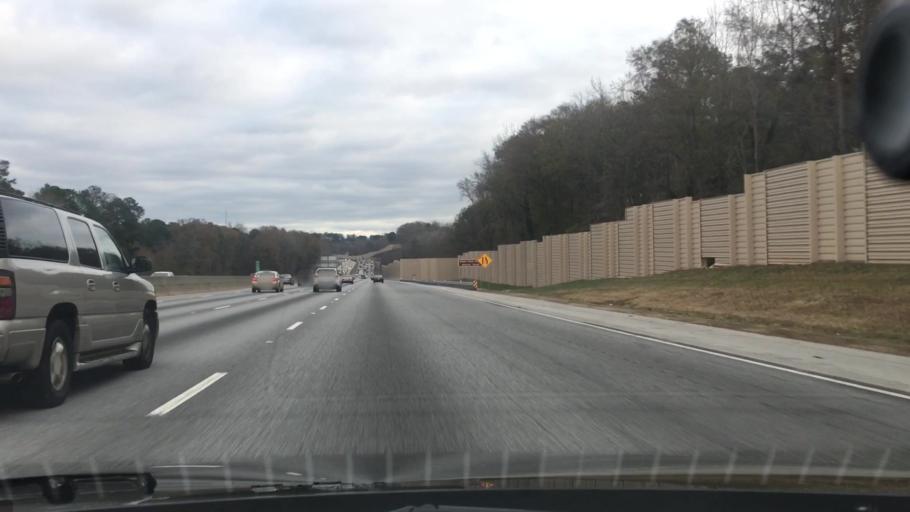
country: US
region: Georgia
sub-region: DeKalb County
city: Panthersville
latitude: 33.7077
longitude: -84.2043
